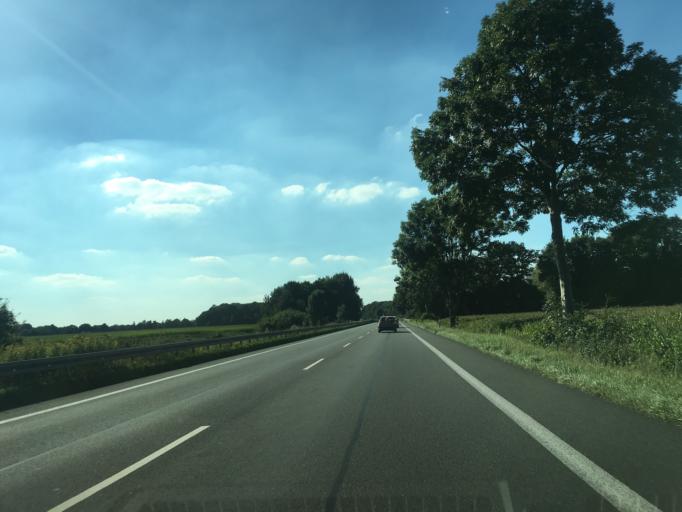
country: DE
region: North Rhine-Westphalia
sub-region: Regierungsbezirk Munster
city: Sassenberg
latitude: 51.9414
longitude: 8.0690
